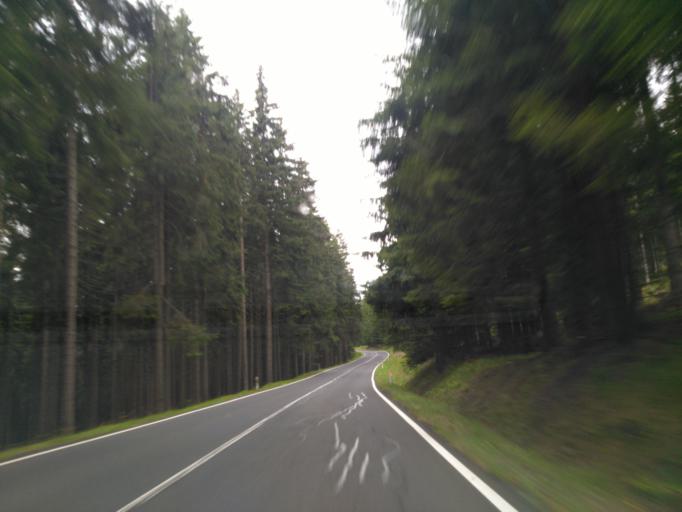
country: CZ
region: Karlovarsky
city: Jachymov
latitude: 50.3832
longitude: 12.8858
